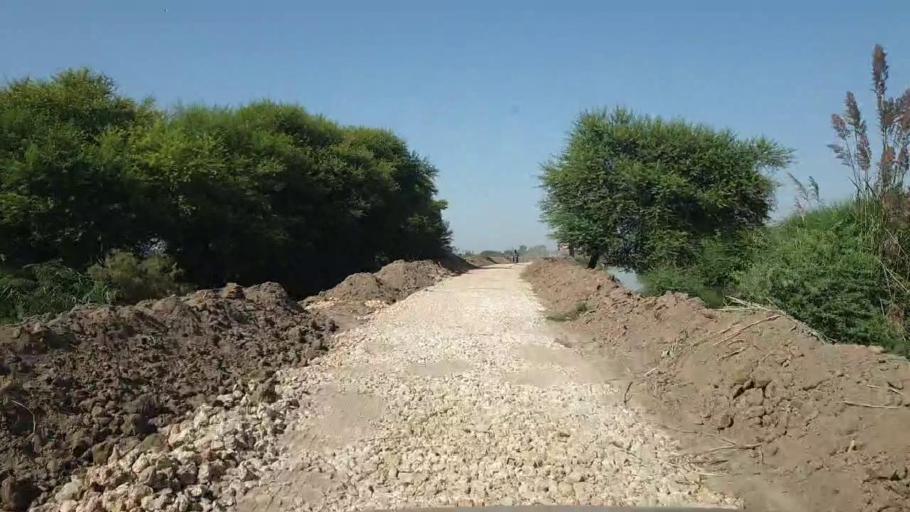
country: PK
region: Sindh
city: Kadhan
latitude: 24.5280
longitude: 69.0007
